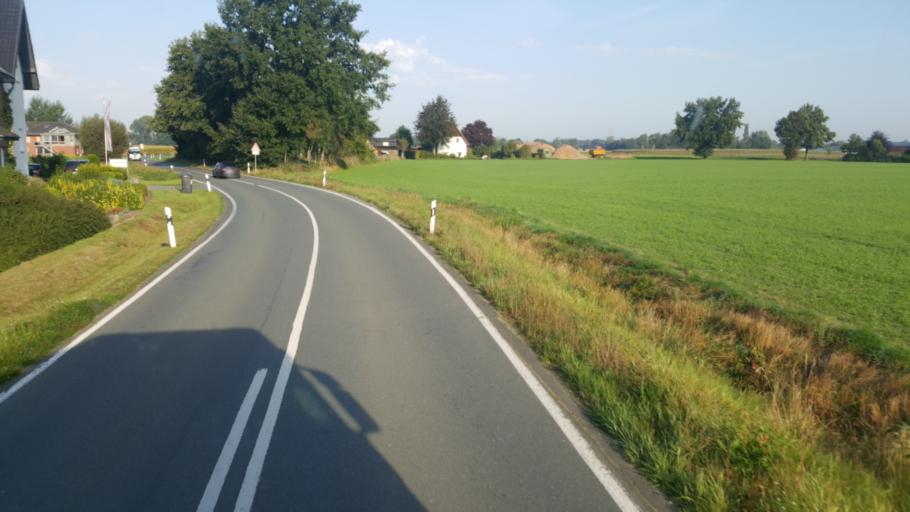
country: DE
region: North Rhine-Westphalia
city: Rietberg
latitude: 51.7393
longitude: 8.3950
